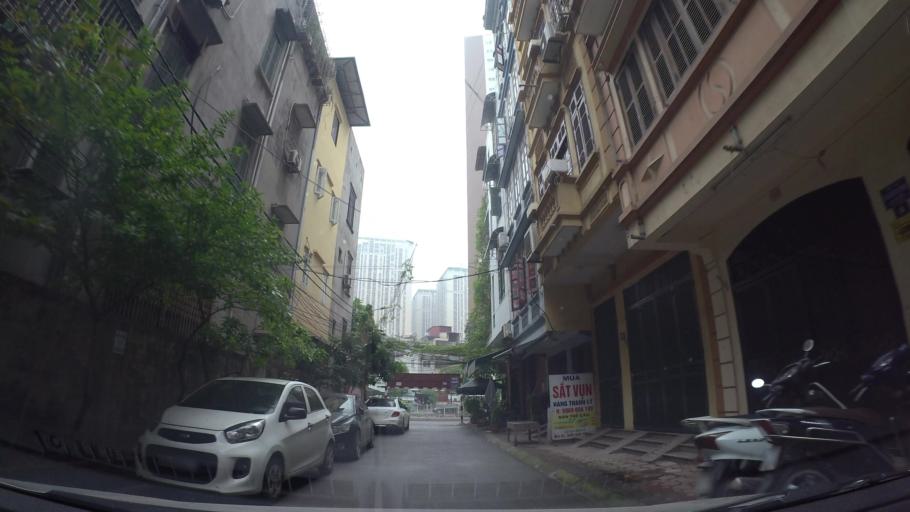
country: VN
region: Ha Noi
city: Cau Giay
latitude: 21.0184
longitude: 105.7907
